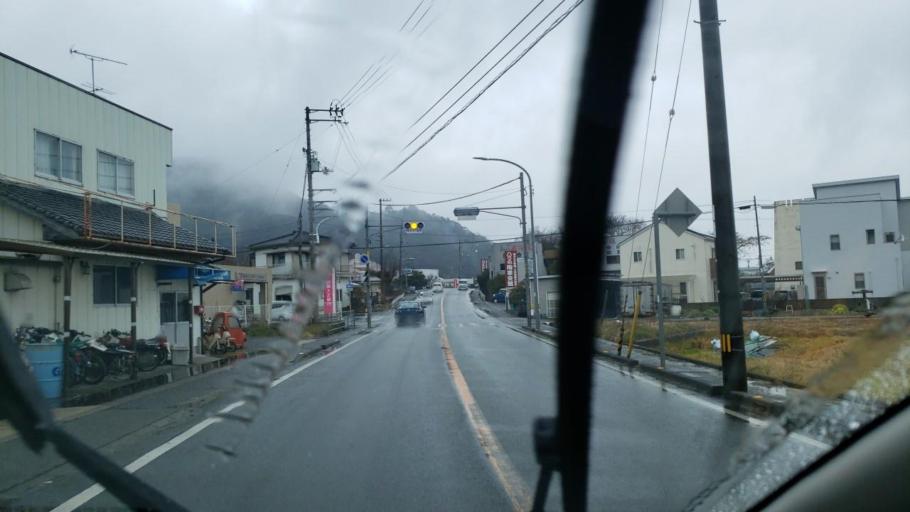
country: JP
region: Tokushima
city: Narutocho-mitsuishi
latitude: 34.1616
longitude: 134.5389
